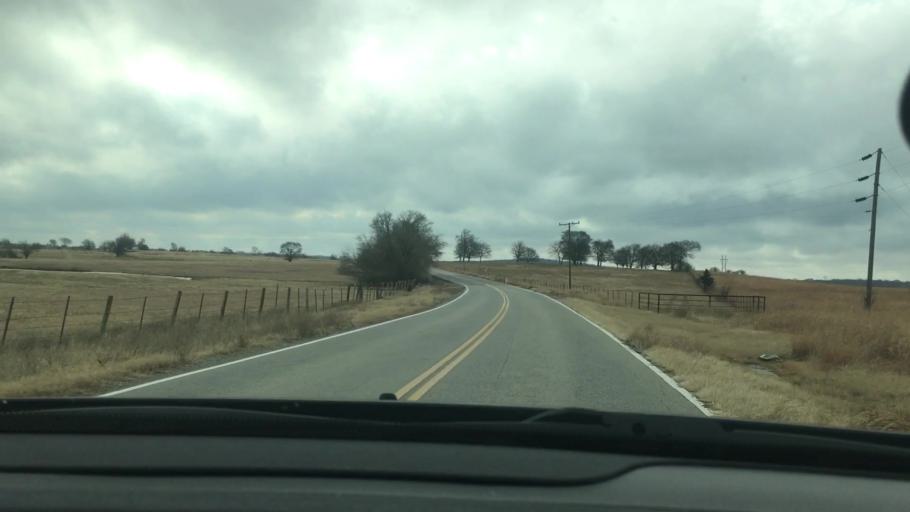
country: US
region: Oklahoma
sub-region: Bryan County
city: Durant
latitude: 34.0965
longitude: -96.4877
